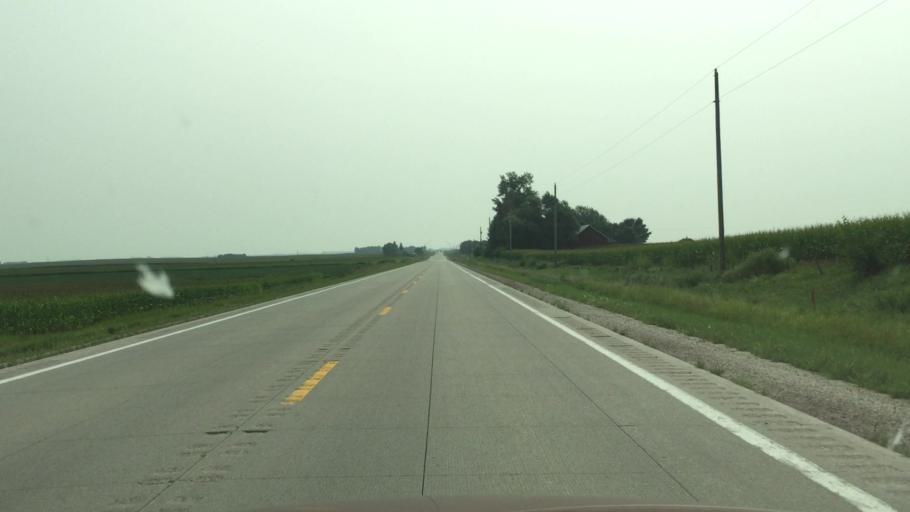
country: US
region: Iowa
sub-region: Osceola County
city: Sibley
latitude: 43.4327
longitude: -95.6526
